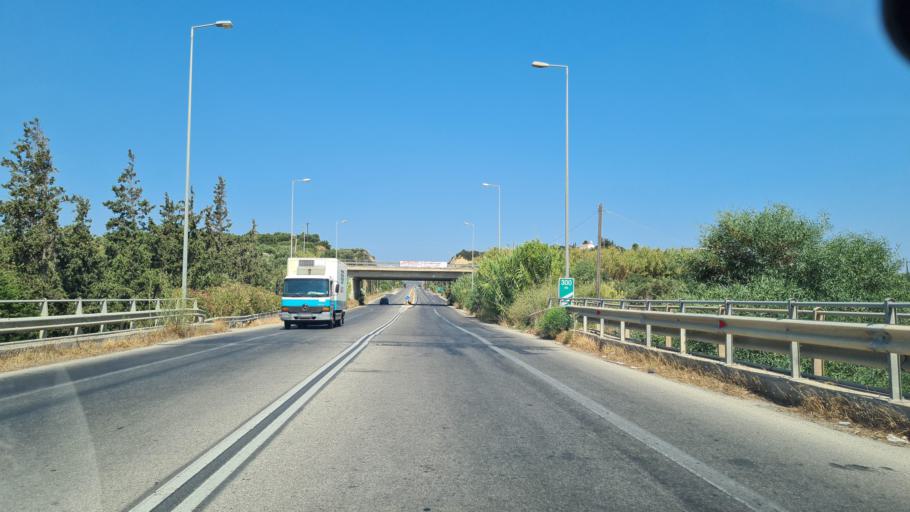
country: GR
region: Crete
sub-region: Nomos Chanias
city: Kolympari
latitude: 35.5187
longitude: 23.8211
